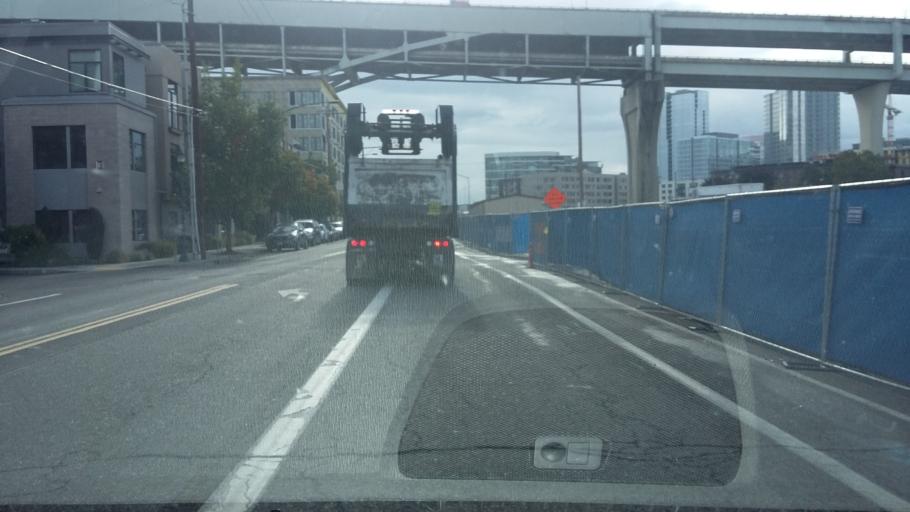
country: US
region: Oregon
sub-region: Multnomah County
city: Portland
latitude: 45.5372
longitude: -122.6873
